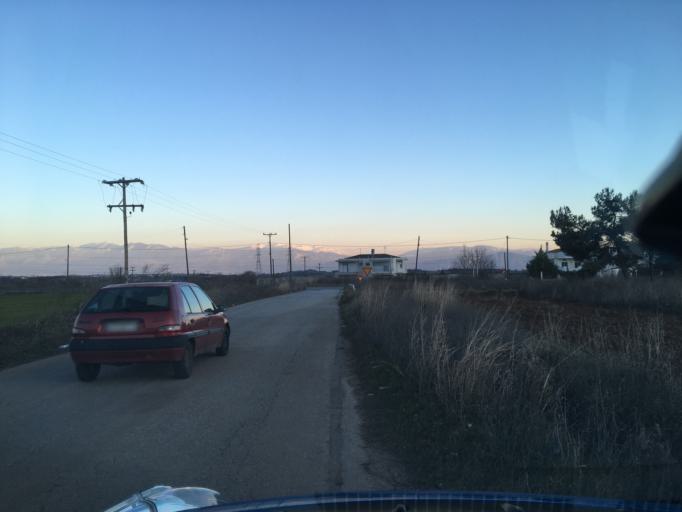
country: GR
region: West Macedonia
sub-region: Nomos Kozanis
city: Kozani
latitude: 40.2570
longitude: 21.7571
